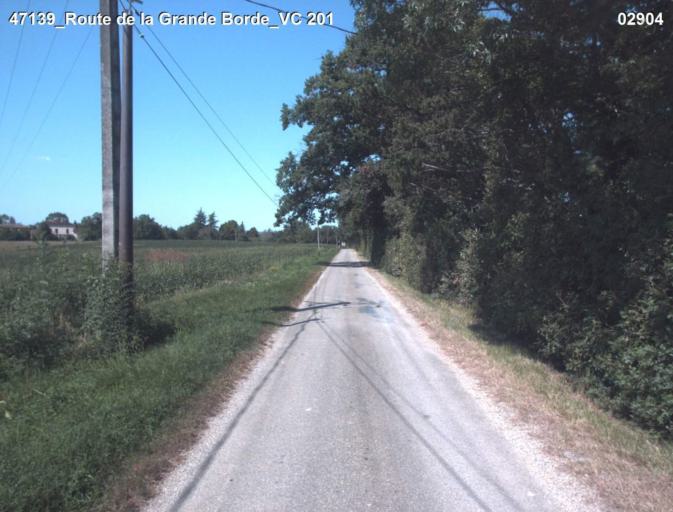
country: FR
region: Aquitaine
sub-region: Departement du Lot-et-Garonne
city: Nerac
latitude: 44.0850
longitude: 0.3815
